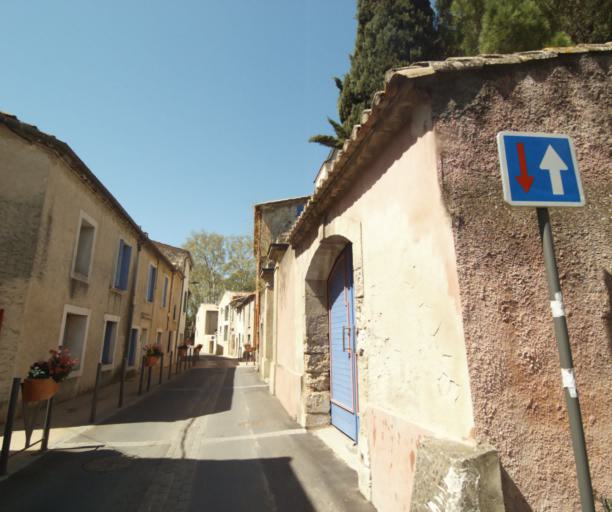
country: FR
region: Languedoc-Roussillon
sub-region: Departement de l'Herault
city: Saint-Bres
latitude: 43.6634
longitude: 4.0309
